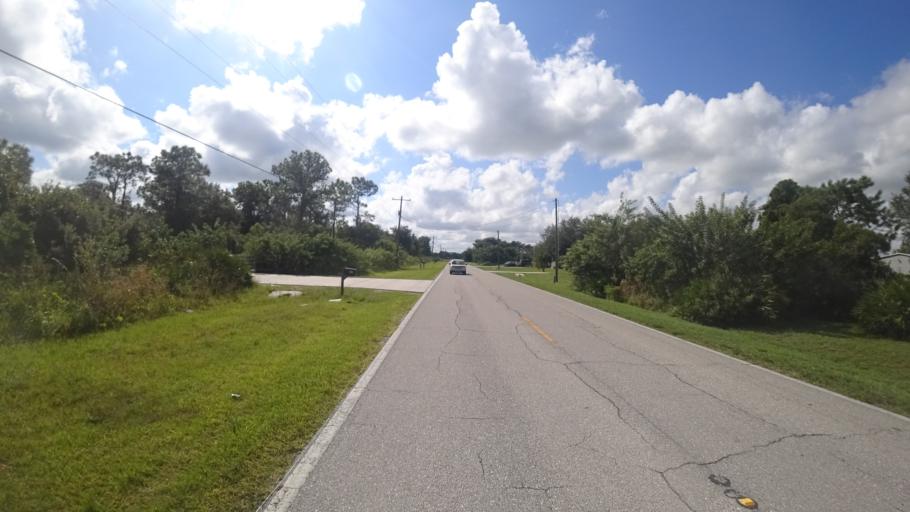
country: US
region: Florida
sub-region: Sarasota County
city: Lake Sarasota
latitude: 27.3912
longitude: -82.2712
